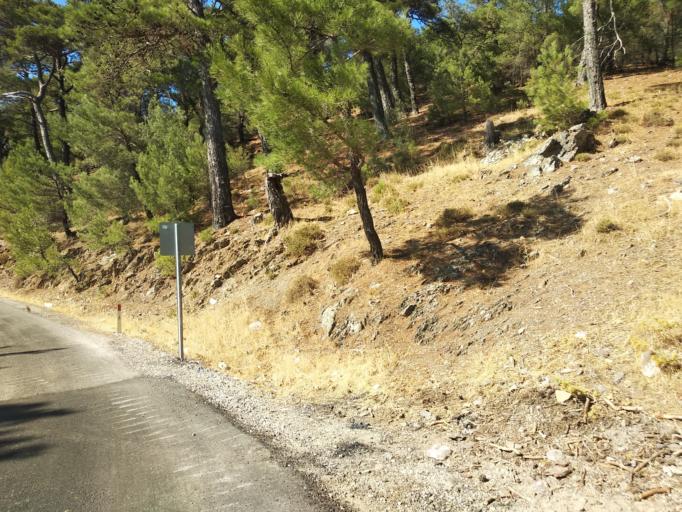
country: TR
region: Izmir
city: Gaziemir
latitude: 38.2981
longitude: 26.9980
